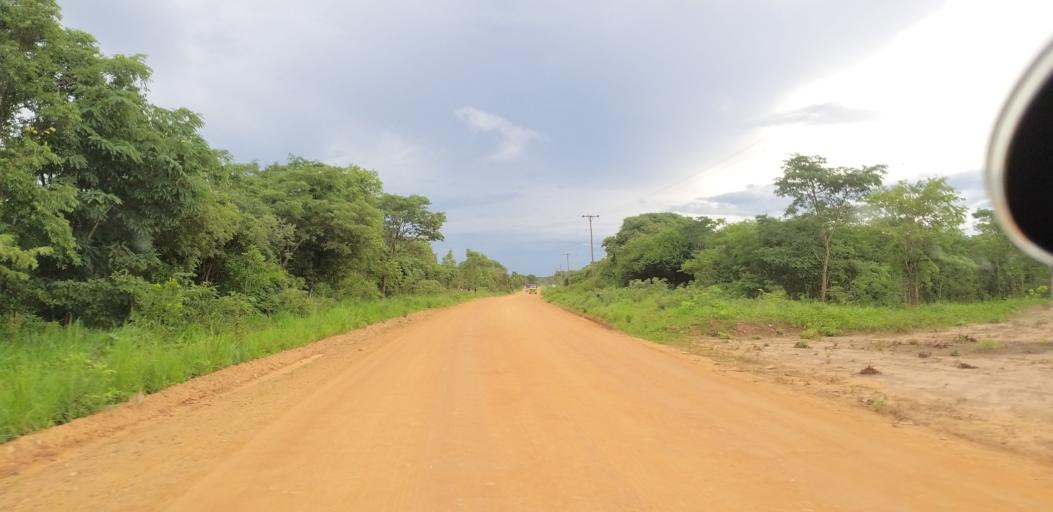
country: ZM
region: Lusaka
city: Chongwe
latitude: -15.1777
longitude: 28.4594
